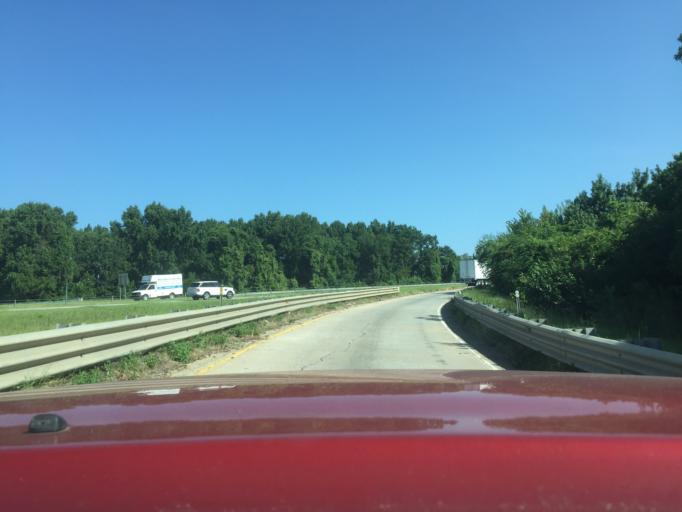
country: US
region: Georgia
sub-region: Chatham County
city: Savannah
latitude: 32.0636
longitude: -81.1373
